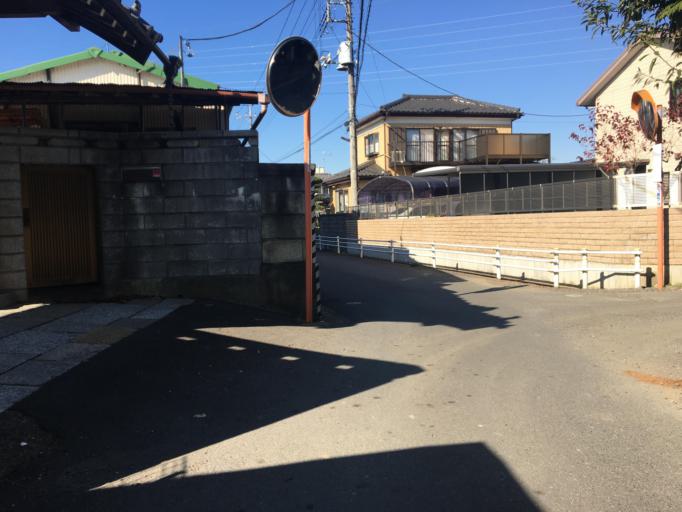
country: JP
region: Saitama
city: Yashio-shi
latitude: 35.8198
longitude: 139.8615
